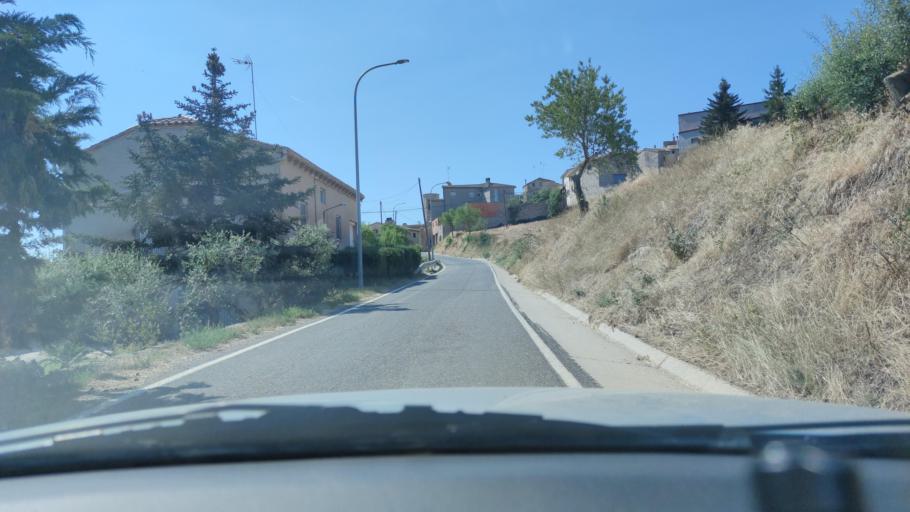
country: ES
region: Catalonia
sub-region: Provincia de Lleida
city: Sant Guim de Freixenet
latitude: 41.6629
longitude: 1.3672
